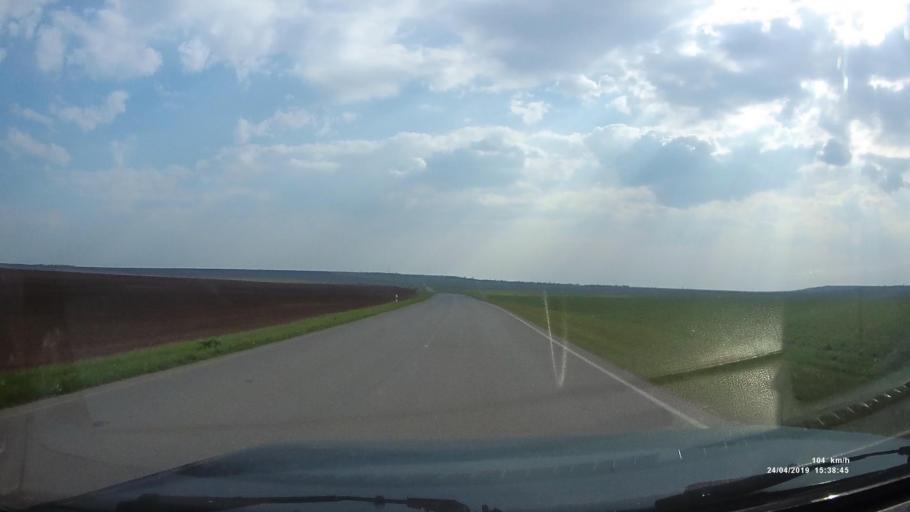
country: RU
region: Kalmykiya
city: Yashalta
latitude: 46.5941
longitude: 42.8233
